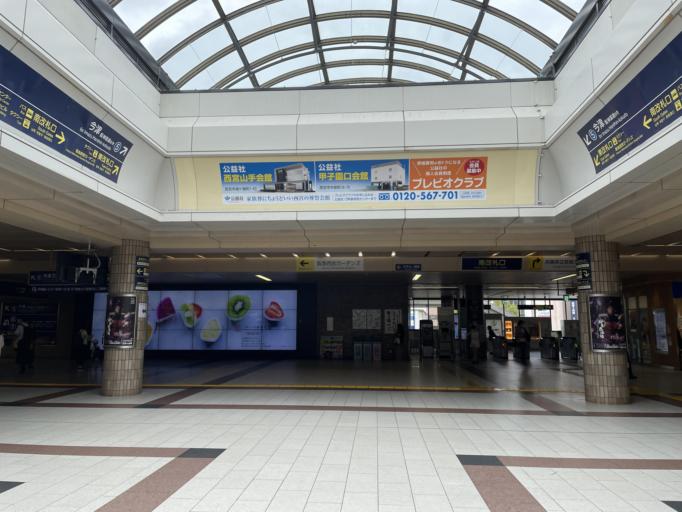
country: JP
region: Hyogo
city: Nishinomiya-hama
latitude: 34.7459
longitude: 135.3567
